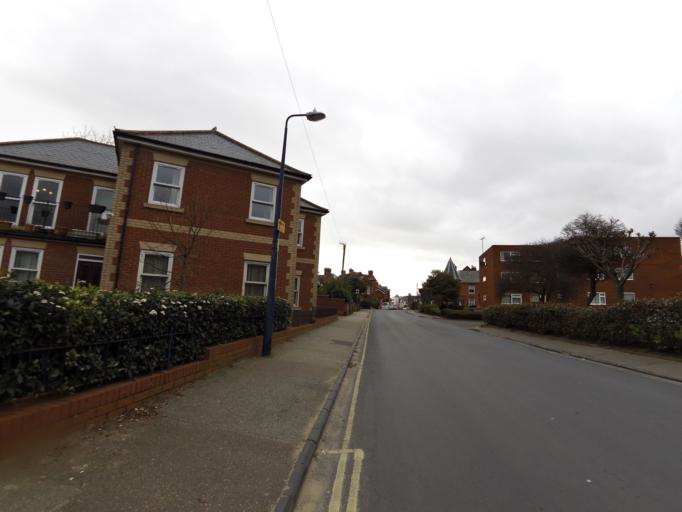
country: GB
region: England
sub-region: Suffolk
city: Felixstowe
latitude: 51.9626
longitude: 1.3568
